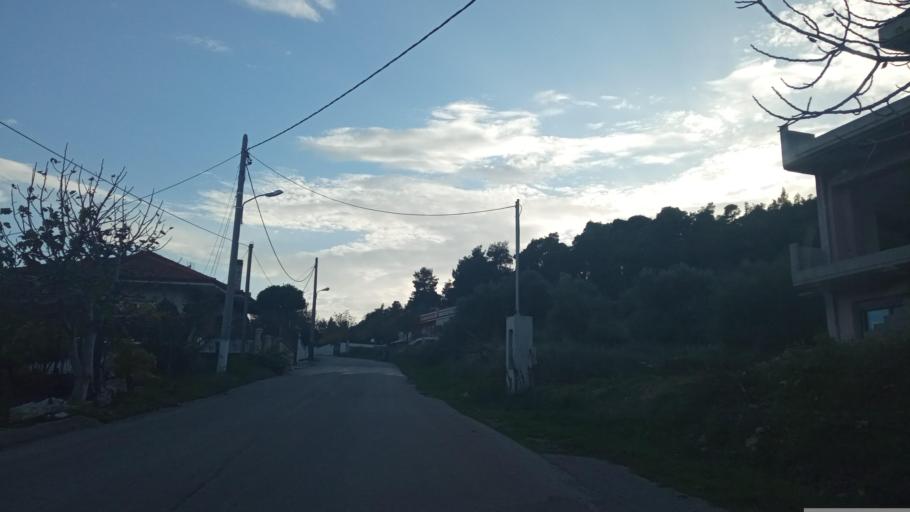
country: GR
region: Central Greece
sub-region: Nomos Evvoias
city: Psachna
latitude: 38.6155
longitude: 23.7322
